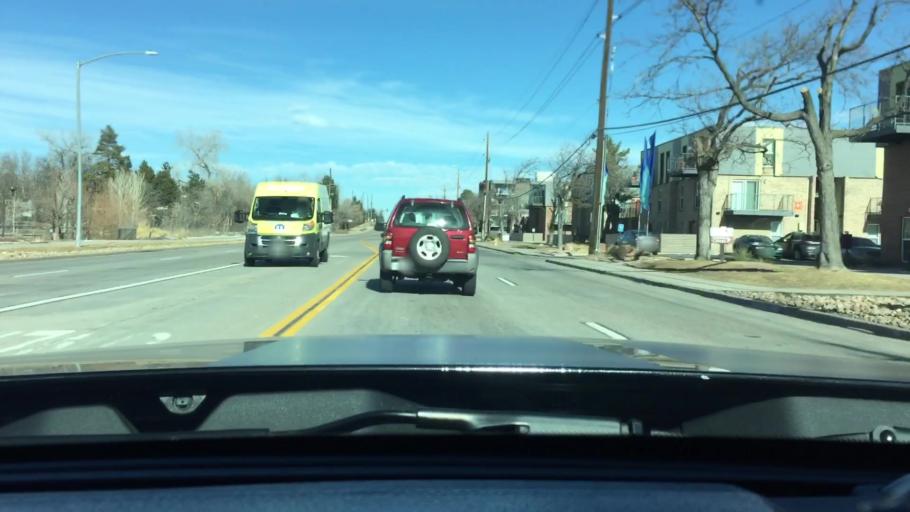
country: US
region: Colorado
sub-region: Adams County
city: Northglenn
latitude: 39.8894
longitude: -104.9967
